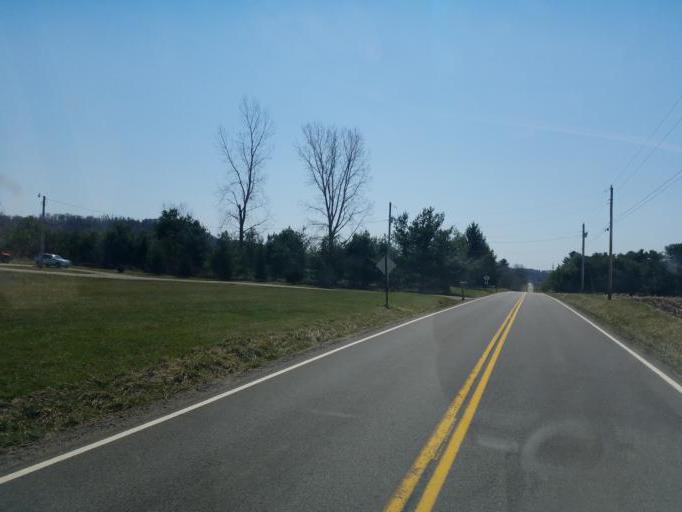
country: US
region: Ohio
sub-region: Ashland County
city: Loudonville
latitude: 40.6966
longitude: -82.2888
